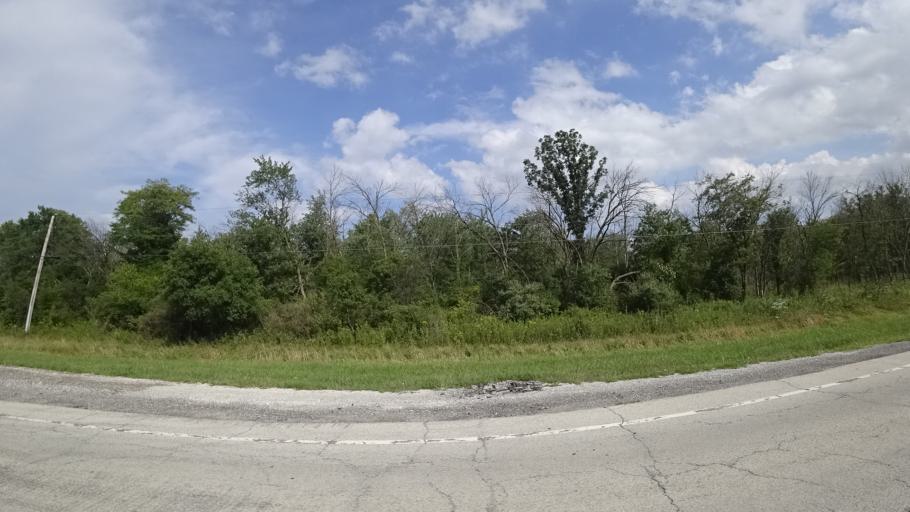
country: US
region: Illinois
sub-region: Cook County
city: Tinley Park
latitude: 41.5510
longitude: -87.7712
